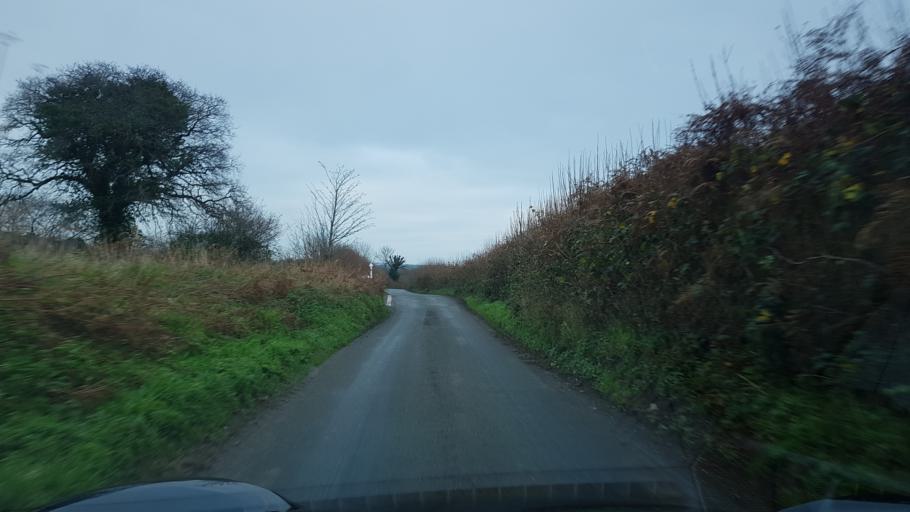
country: GB
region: England
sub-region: Somerset
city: Chard
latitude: 50.9012
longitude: -2.9624
